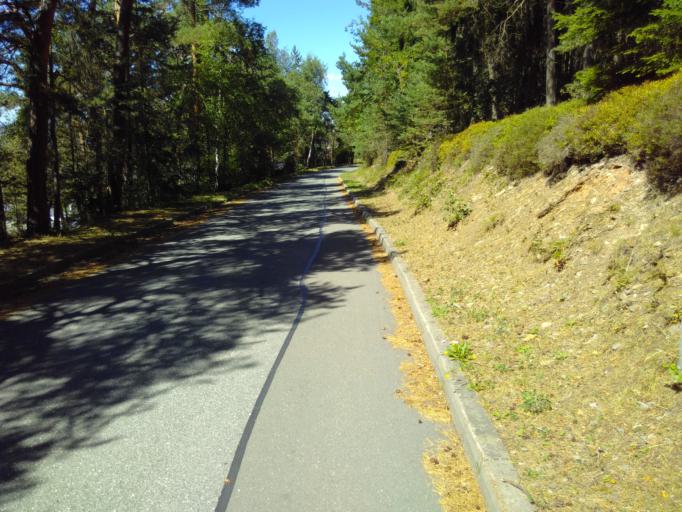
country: DE
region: Thuringia
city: Oberweissbach
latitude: 50.5896
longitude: 11.1334
